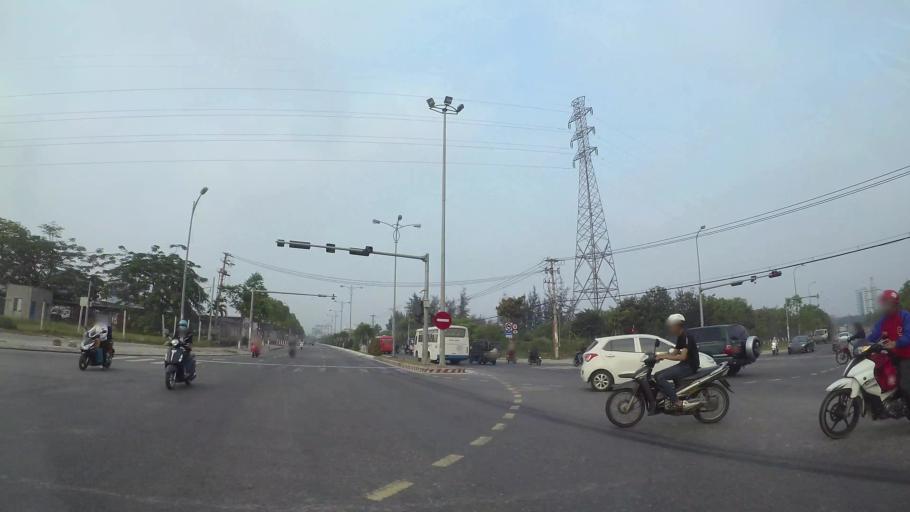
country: VN
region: Da Nang
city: Cam Le
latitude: 16.0260
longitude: 108.2209
